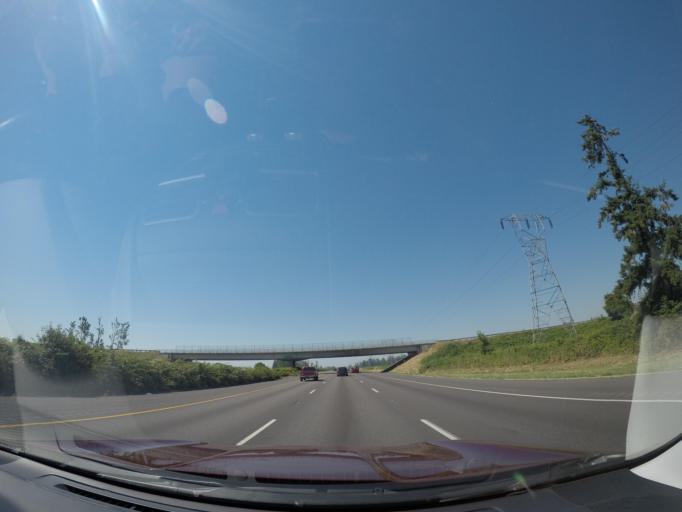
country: US
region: Oregon
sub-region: Marion County
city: Gervais
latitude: 45.1161
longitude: -122.9167
